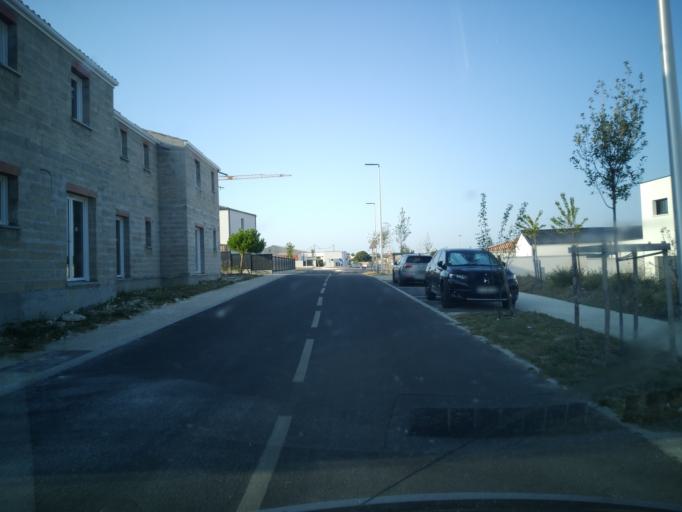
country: FR
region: Poitou-Charentes
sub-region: Departement de la Charente-Maritime
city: Vaux-sur-Mer
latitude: 45.6396
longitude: -1.0541
